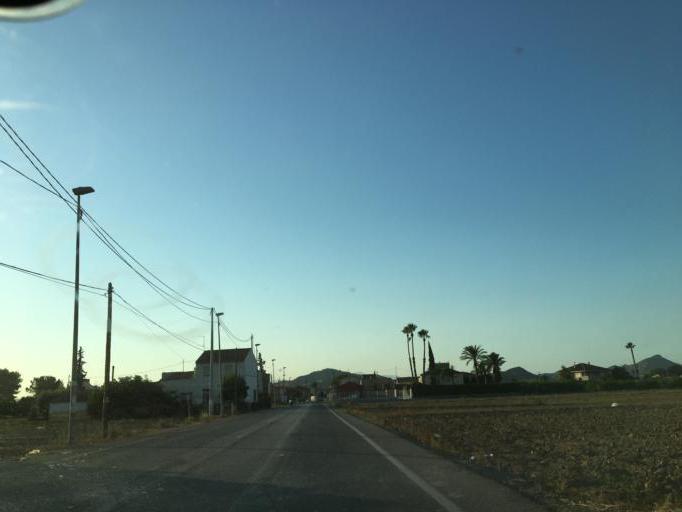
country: ES
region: Murcia
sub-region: Murcia
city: Murcia
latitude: 38.0041
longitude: -1.0778
